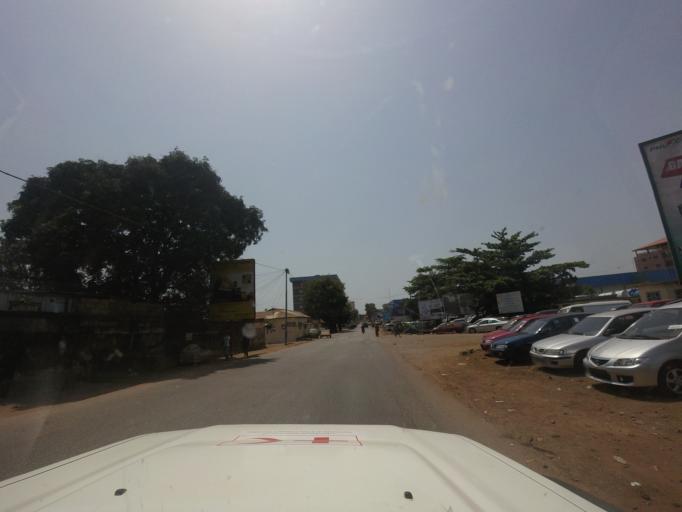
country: GN
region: Conakry
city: Camayenne
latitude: 9.5175
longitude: -13.6993
